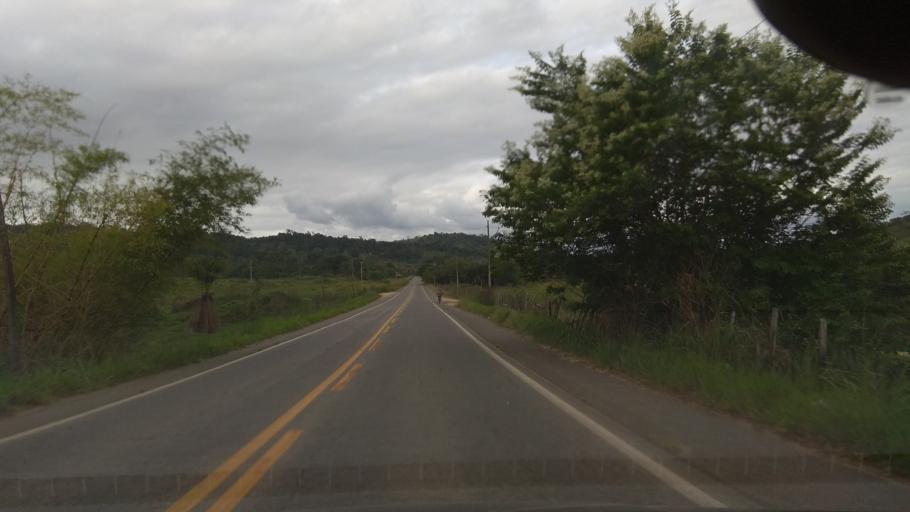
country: BR
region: Bahia
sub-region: Ipiau
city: Ipiau
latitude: -14.1449
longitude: -39.7131
